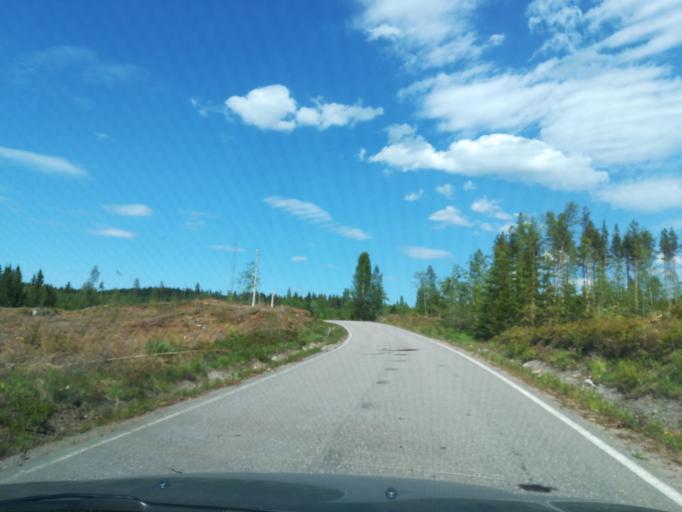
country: FI
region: South Karelia
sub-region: Imatra
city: Ruokolahti
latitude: 61.4749
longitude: 28.8704
